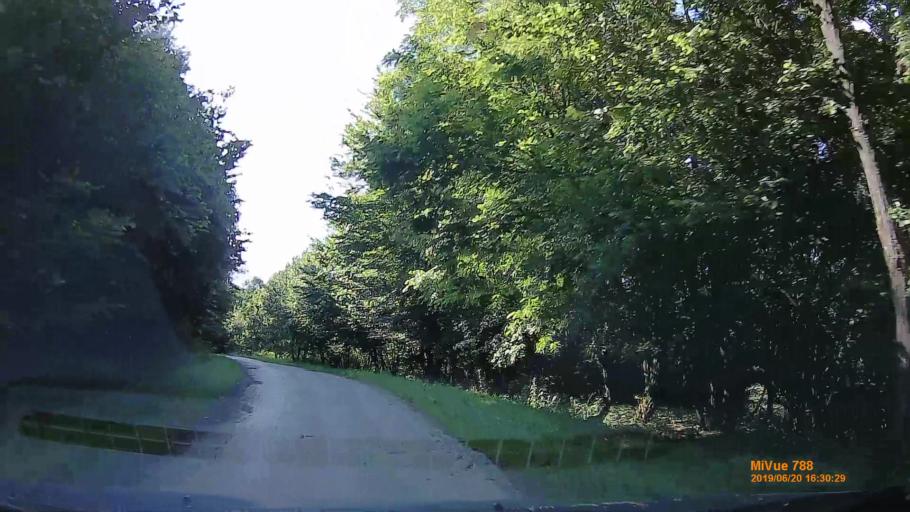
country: HU
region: Baranya
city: Buekkoesd
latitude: 46.1694
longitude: 18.0559
